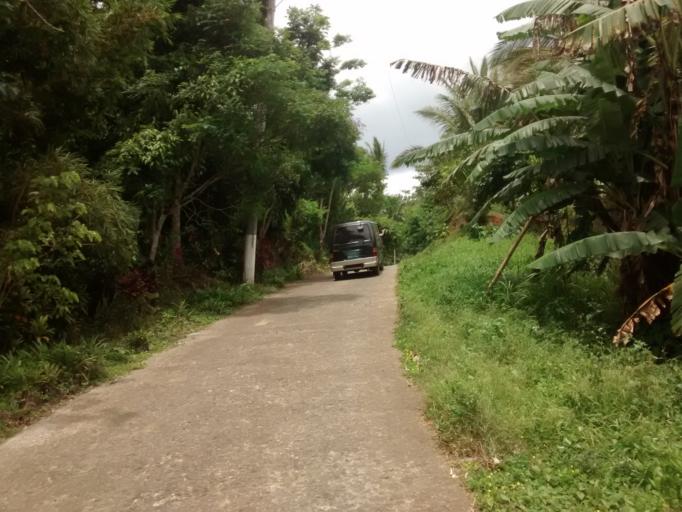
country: PH
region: Calabarzon
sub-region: Province of Quezon
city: Lucban
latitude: 14.1558
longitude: 121.5550
